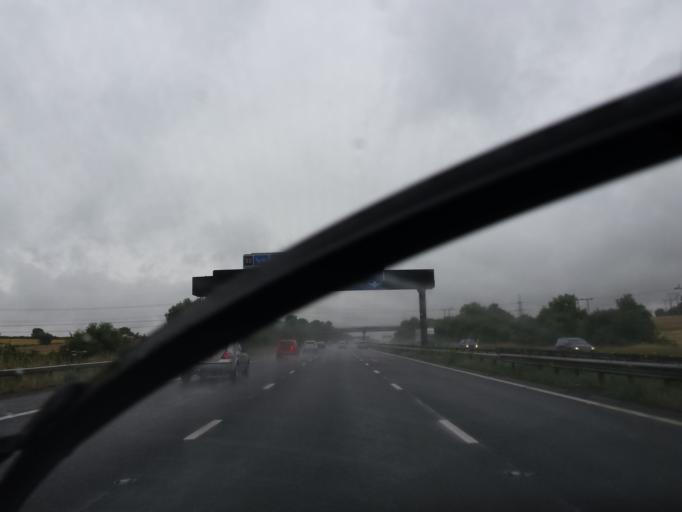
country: GB
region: England
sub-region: Rotherham
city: Bramley
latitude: 53.4093
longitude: -1.2584
